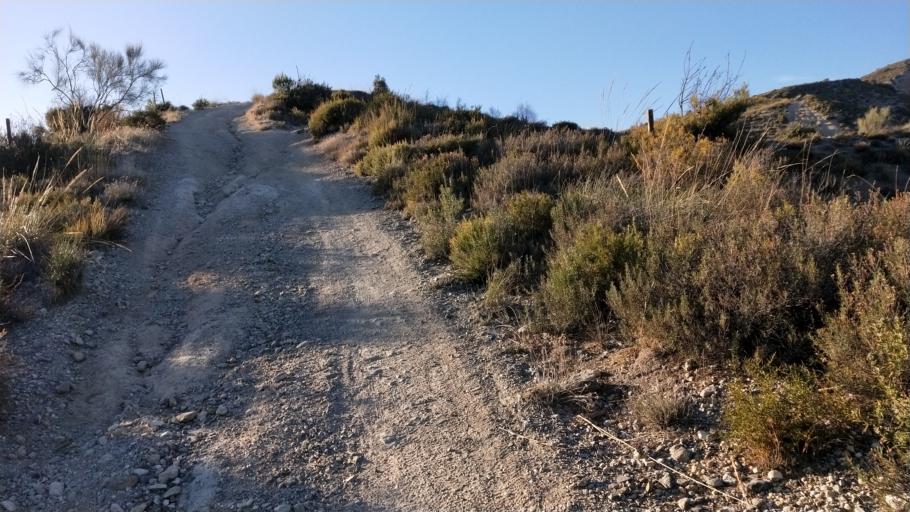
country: ES
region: Andalusia
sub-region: Provincia de Granada
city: Dudar
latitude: 37.1926
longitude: -3.4975
